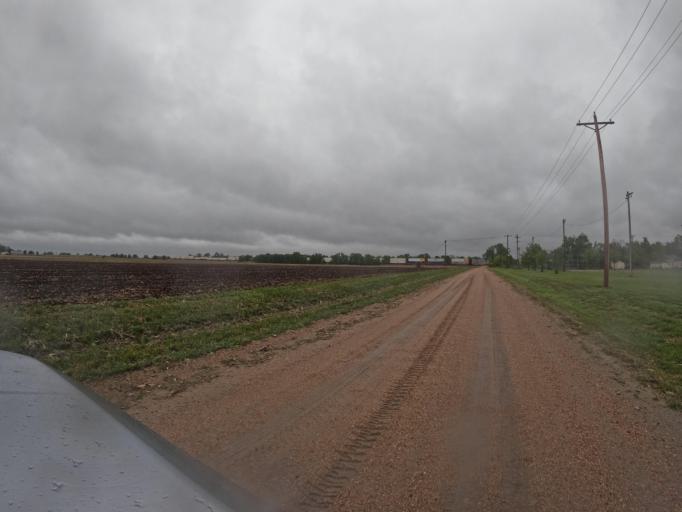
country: US
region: Nebraska
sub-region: Clay County
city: Harvard
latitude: 40.6143
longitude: -98.1027
